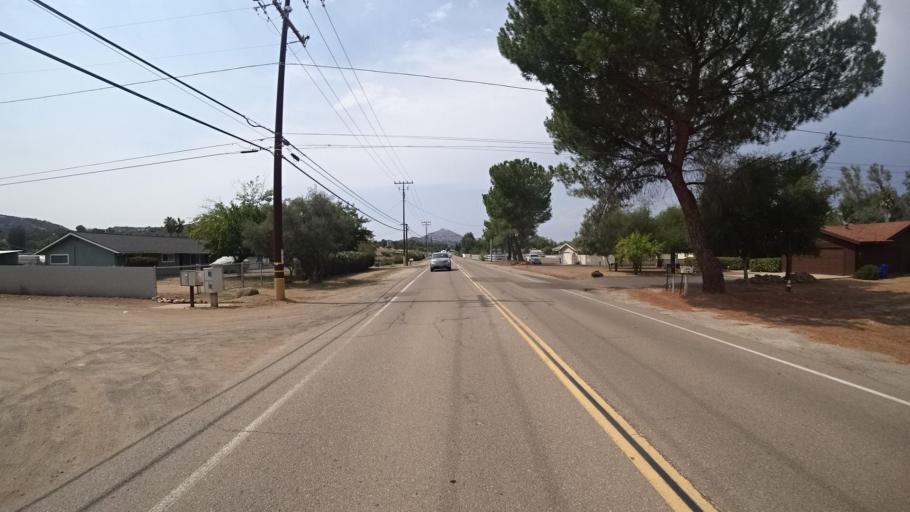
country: US
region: California
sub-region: San Diego County
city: Ramona
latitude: 33.0084
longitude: -116.8990
